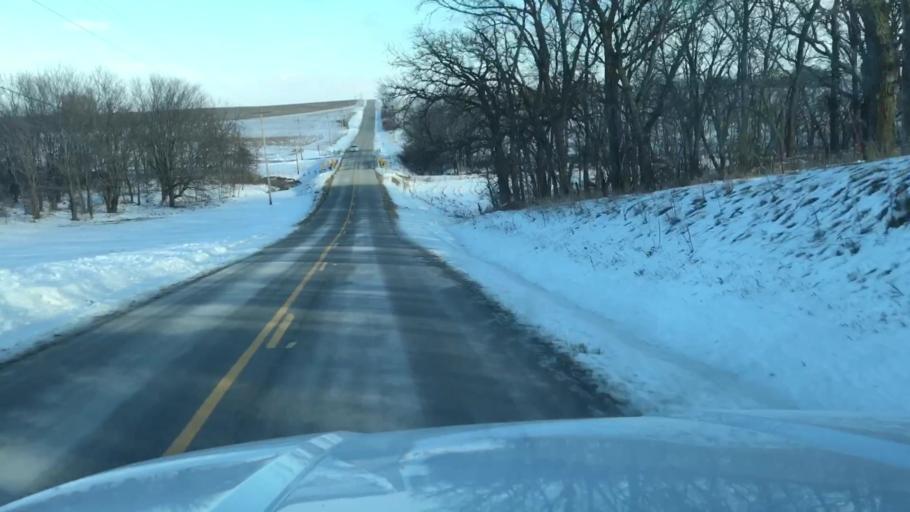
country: US
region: Missouri
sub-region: Holt County
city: Oregon
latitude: 40.1007
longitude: -95.0050
